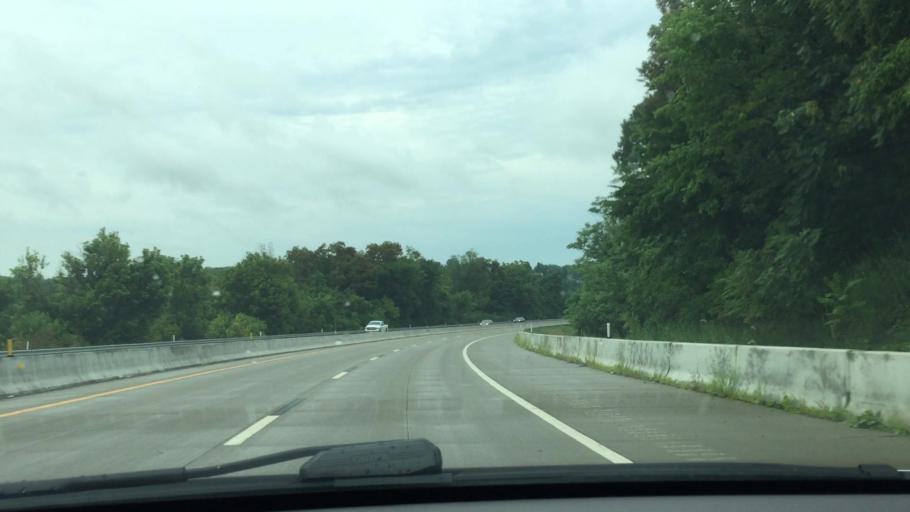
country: US
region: Pennsylvania
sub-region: Allegheny County
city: Bridgeville
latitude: 40.3510
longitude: -80.1473
